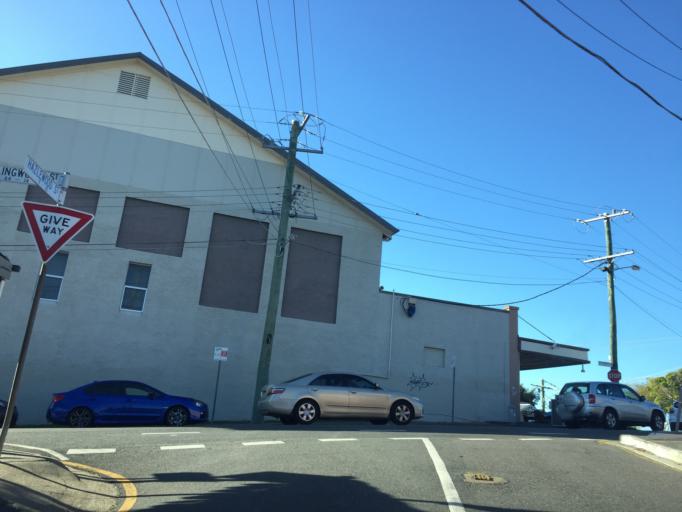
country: AU
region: Queensland
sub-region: Brisbane
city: Milton
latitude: -27.4581
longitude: 152.9943
